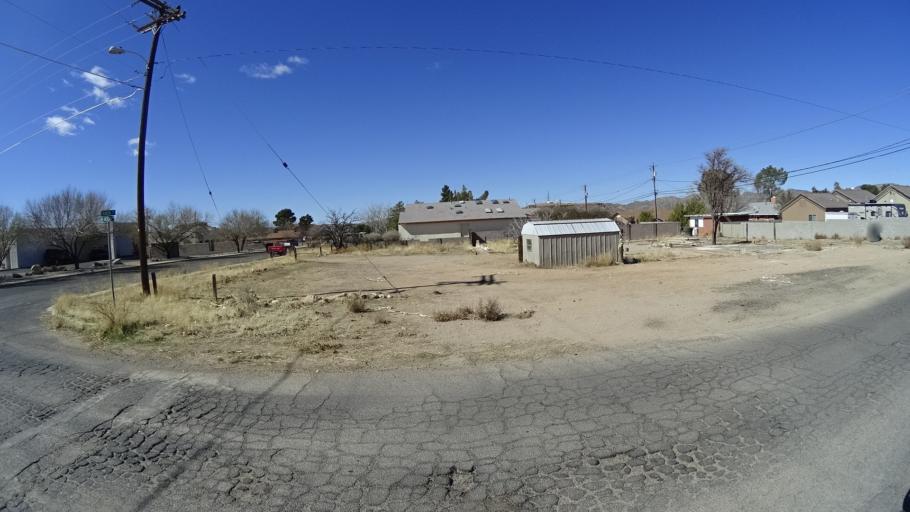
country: US
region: Arizona
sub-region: Mohave County
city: Kingman
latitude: 35.1923
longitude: -114.0202
